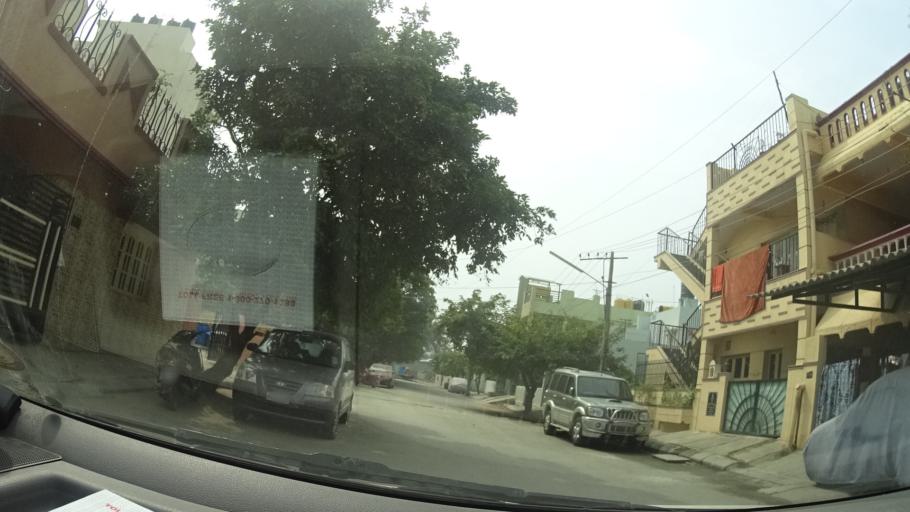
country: IN
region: Karnataka
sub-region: Bangalore Urban
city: Bangalore
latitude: 13.0290
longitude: 77.6241
